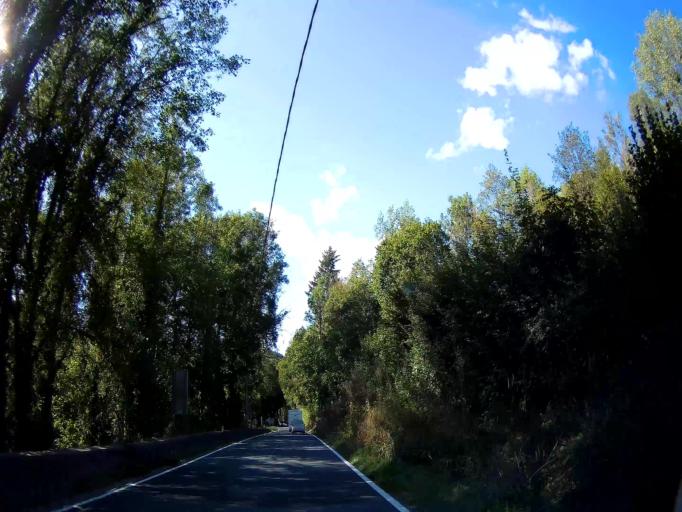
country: BE
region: Wallonia
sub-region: Province de Namur
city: Onhaye
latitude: 50.3063
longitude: 4.7681
